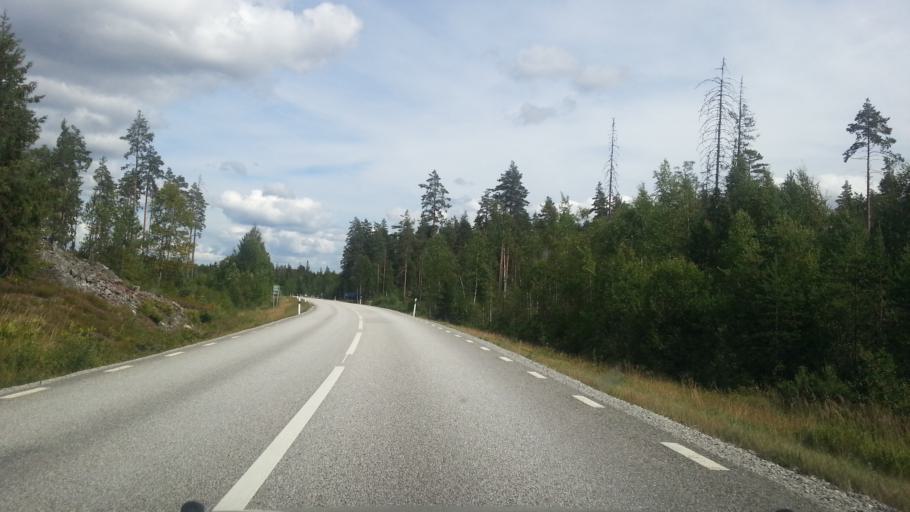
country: SE
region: Vaestmanland
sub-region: Skinnskattebergs Kommun
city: Skinnskatteberg
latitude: 59.7686
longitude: 15.5174
